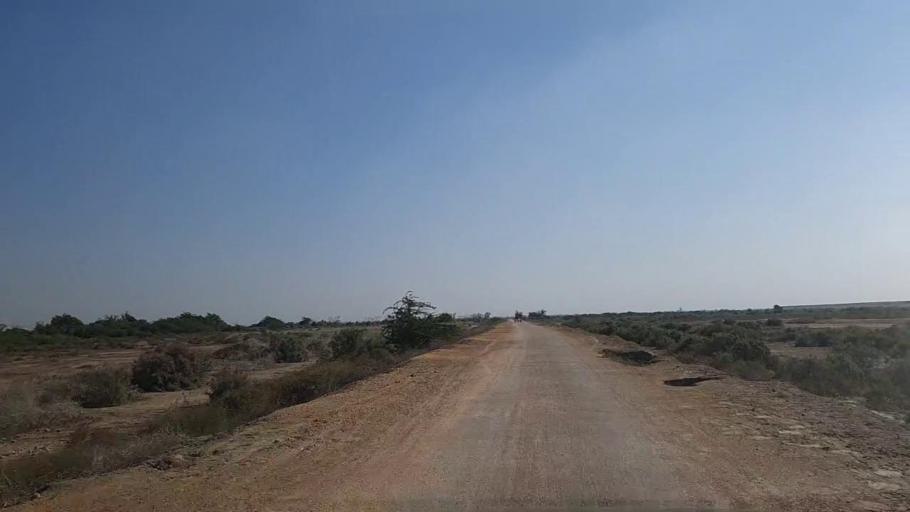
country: PK
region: Sindh
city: Daro Mehar
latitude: 24.8031
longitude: 68.0770
